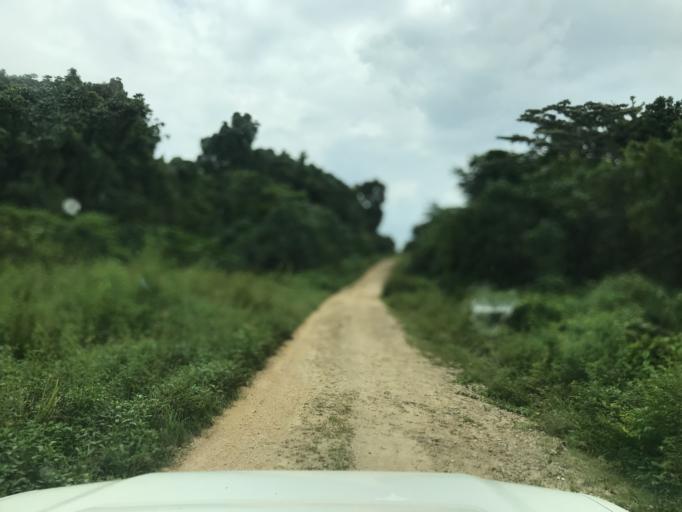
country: VU
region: Sanma
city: Port-Olry
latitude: -15.1877
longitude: 167.0055
